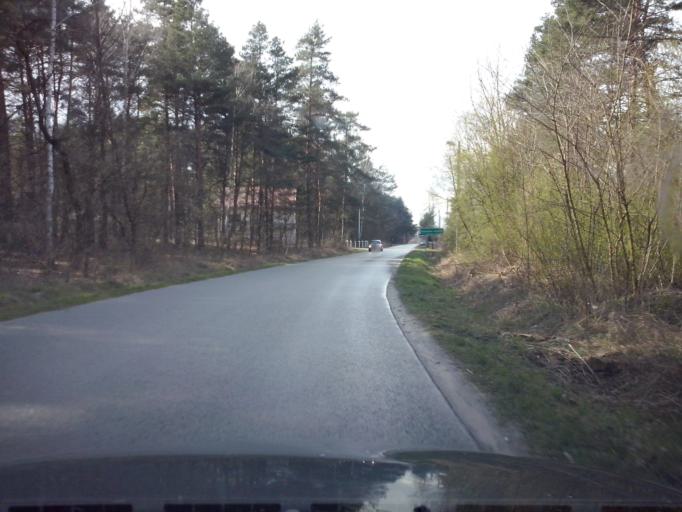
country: PL
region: Subcarpathian Voivodeship
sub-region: Powiat nizanski
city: Krzeszow
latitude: 50.4149
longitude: 22.3377
